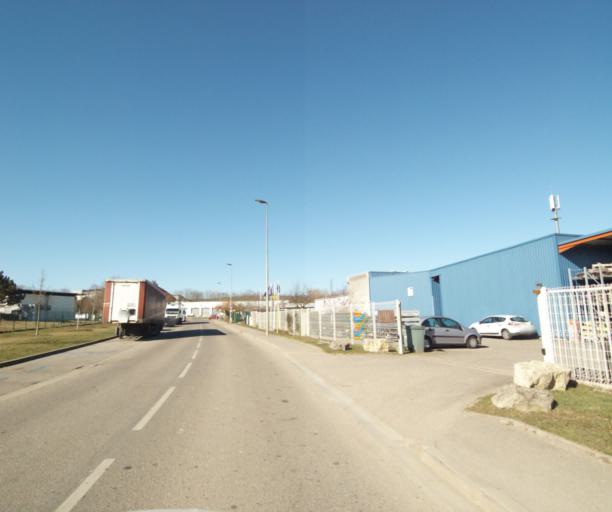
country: FR
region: Lorraine
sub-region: Departement de Meurthe-et-Moselle
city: Fleville-devant-Nancy
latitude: 48.6144
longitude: 6.2046
